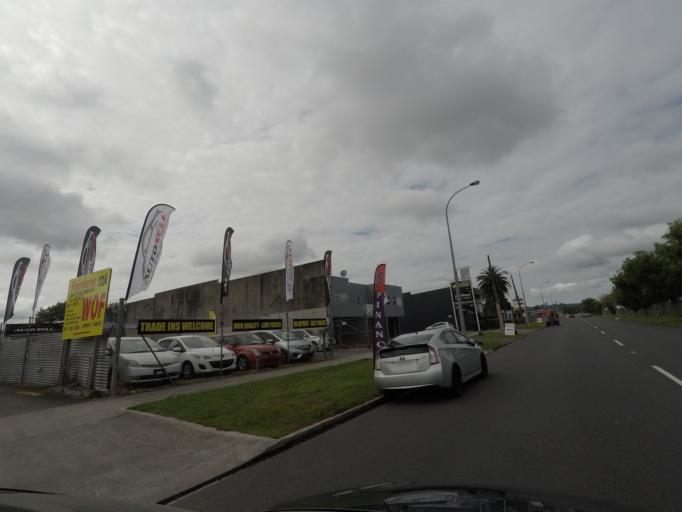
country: NZ
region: Auckland
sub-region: Auckland
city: Waitakere
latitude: -36.8874
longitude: 174.6316
